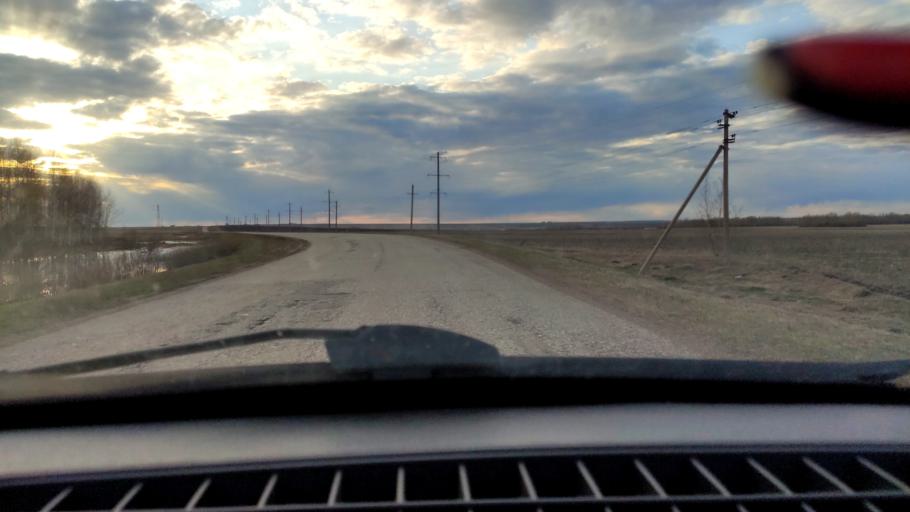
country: RU
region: Bashkortostan
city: Tolbazy
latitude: 54.0084
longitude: 55.7526
